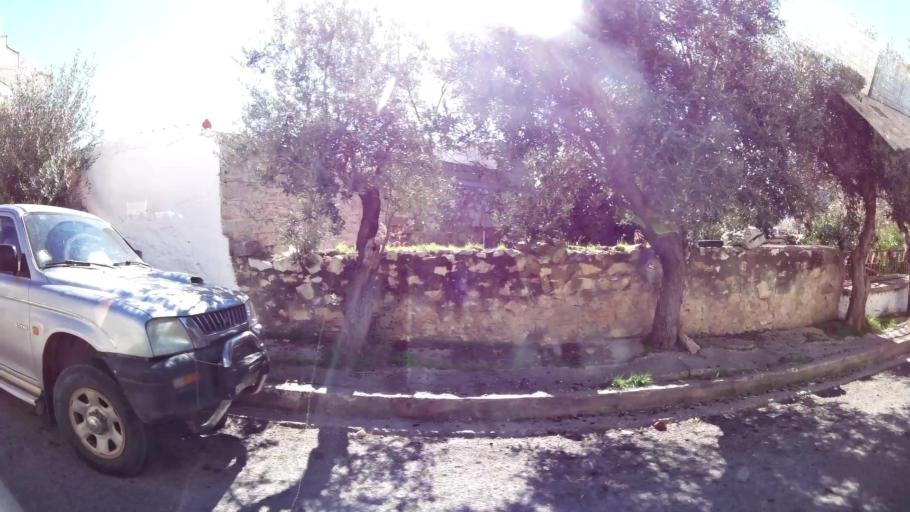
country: GR
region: Attica
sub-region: Nomarchia Anatolikis Attikis
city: Koropi
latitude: 37.8997
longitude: 23.8808
